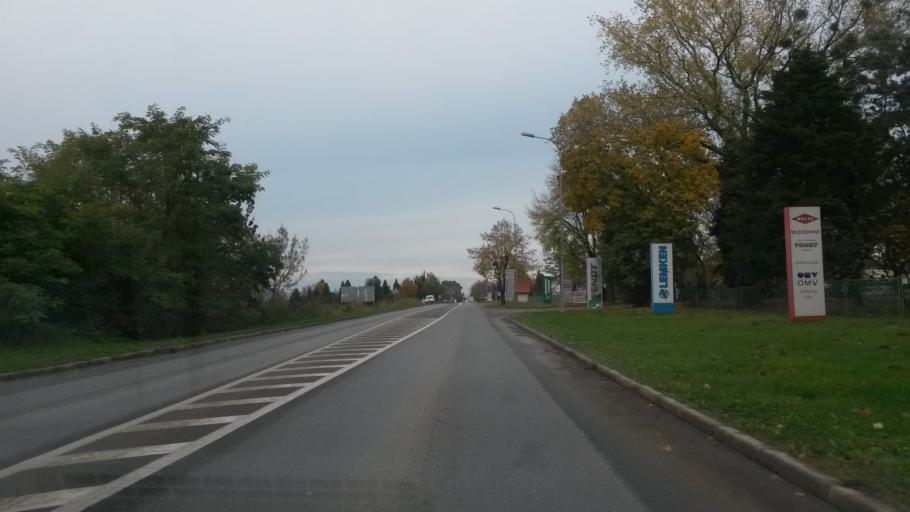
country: HR
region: Osjecko-Baranjska
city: Beli Manastir
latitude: 45.7616
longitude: 18.6254
